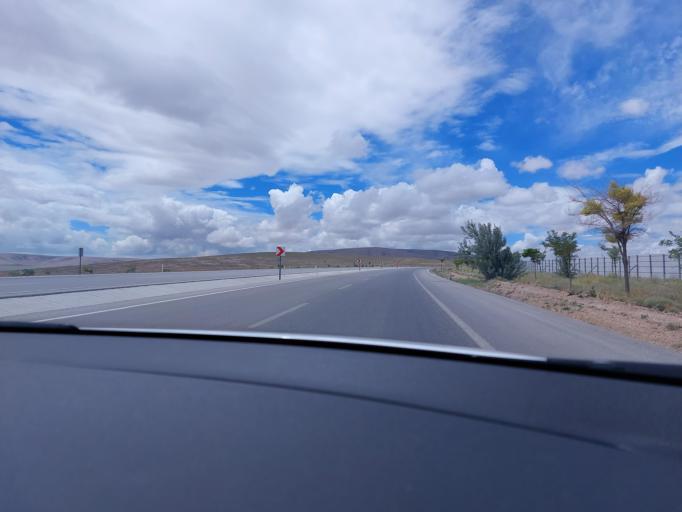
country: TR
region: Konya
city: Obruk
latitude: 38.0648
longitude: 33.0608
